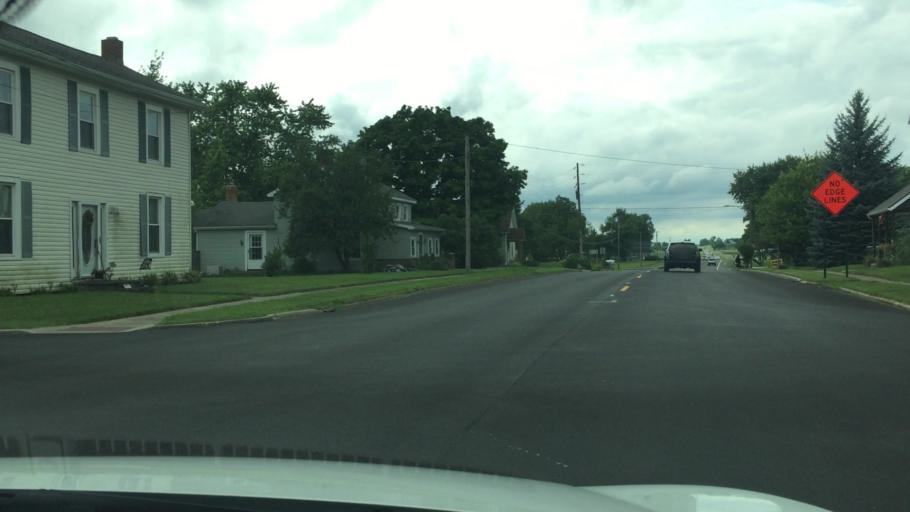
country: US
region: Ohio
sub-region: Champaign County
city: Mechanicsburg
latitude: 40.0788
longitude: -83.6395
